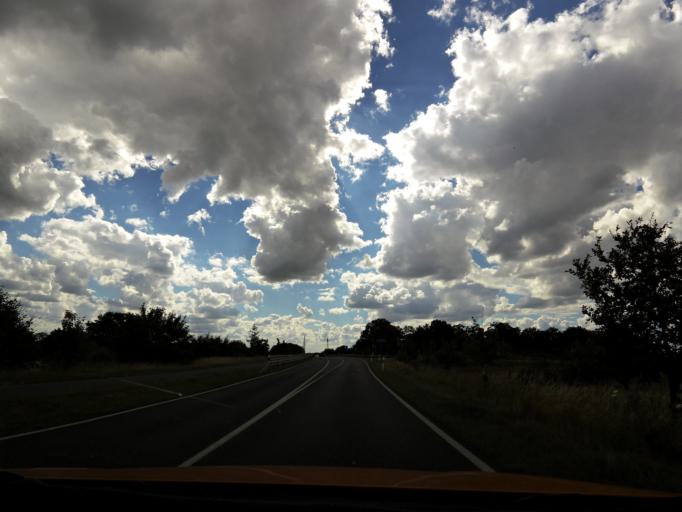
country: DE
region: Brandenburg
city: Mittenwalde
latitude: 52.2920
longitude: 13.5628
